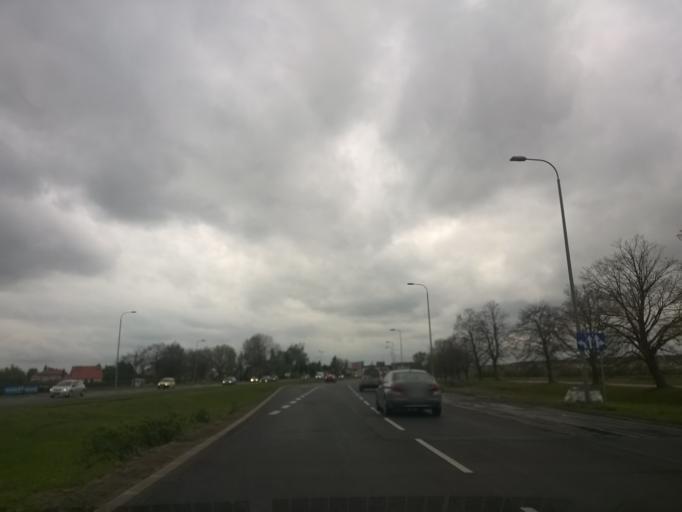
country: PL
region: Masovian Voivodeship
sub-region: Warszawa
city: Kabaty
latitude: 52.1356
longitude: 21.1000
